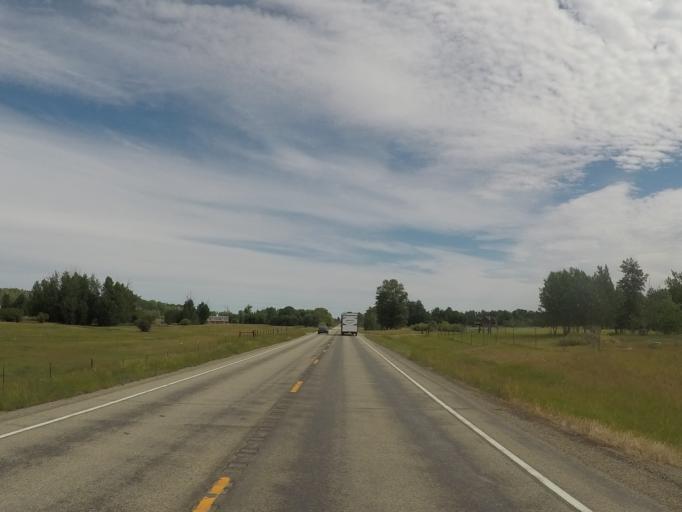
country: US
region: Montana
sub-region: Carbon County
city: Red Lodge
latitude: 45.2644
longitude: -109.2249
